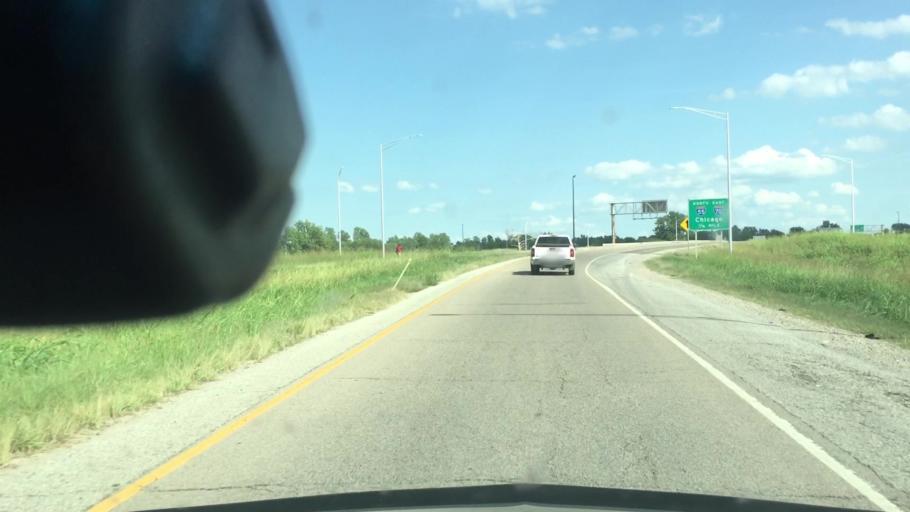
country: US
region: Illinois
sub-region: Saint Clair County
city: East Saint Louis
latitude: 38.6470
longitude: -90.1304
